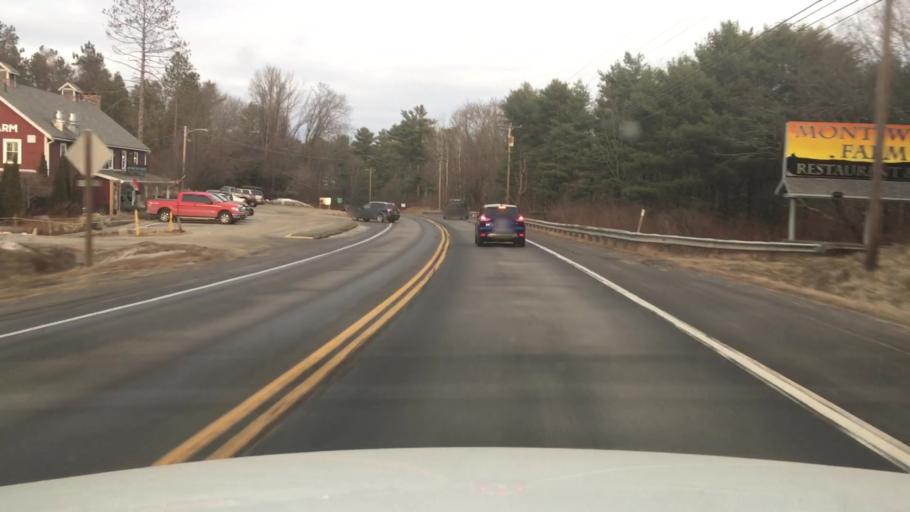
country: US
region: Maine
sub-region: Lincoln County
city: Wiscasset
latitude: 43.9632
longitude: -69.7225
